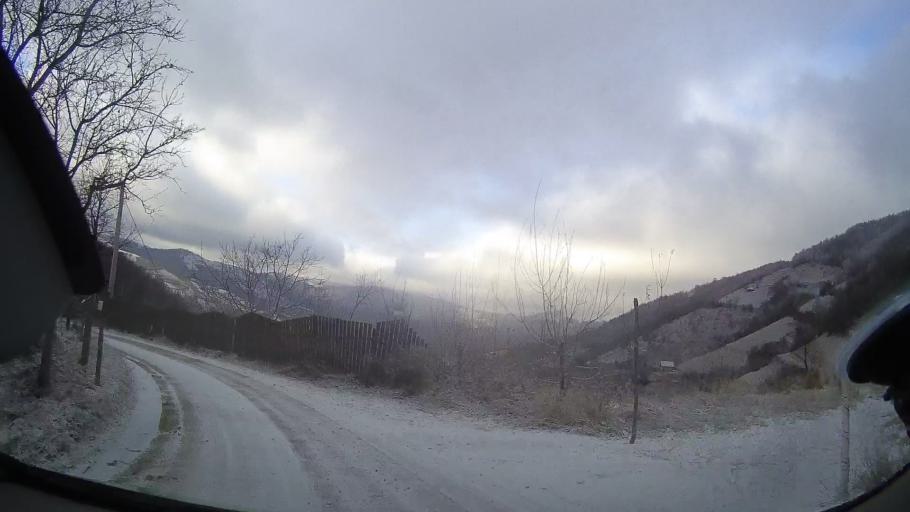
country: RO
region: Cluj
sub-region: Comuna Valea Ierii
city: Valea Ierii
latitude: 46.6664
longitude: 23.3324
